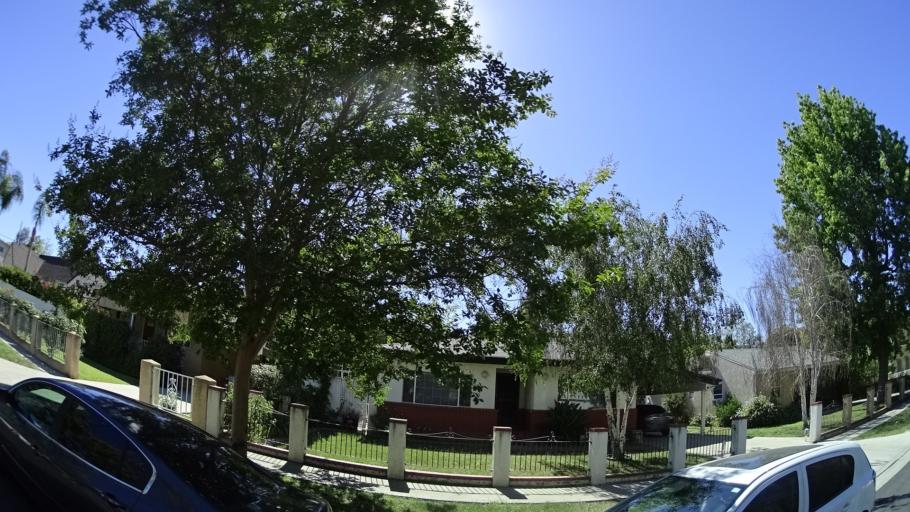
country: US
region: California
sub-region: Los Angeles County
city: Sherman Oaks
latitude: 34.1546
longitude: -118.4585
